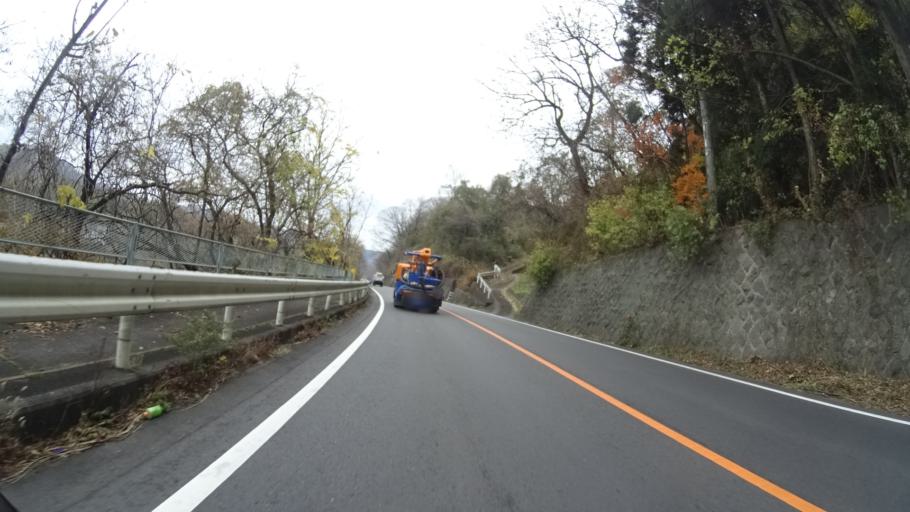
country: JP
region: Gunma
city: Numata
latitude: 36.6089
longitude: 139.0426
